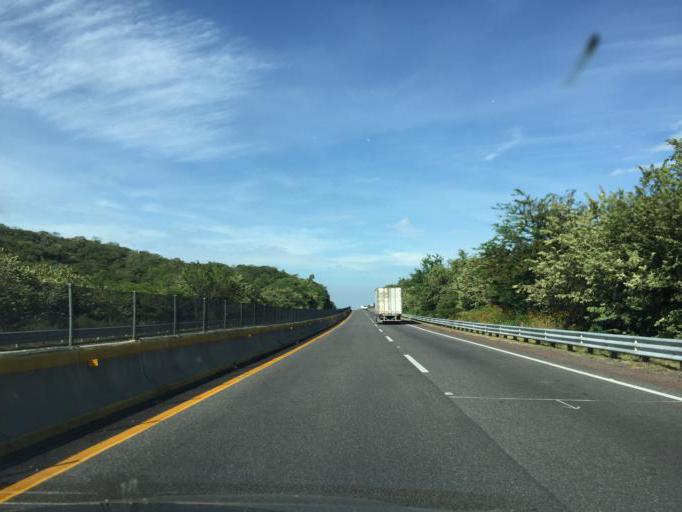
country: MX
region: Guerrero
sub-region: Huitzuco de los Figueroa
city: Ciudad de Huitzuco
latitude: 18.2894
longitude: -99.2075
